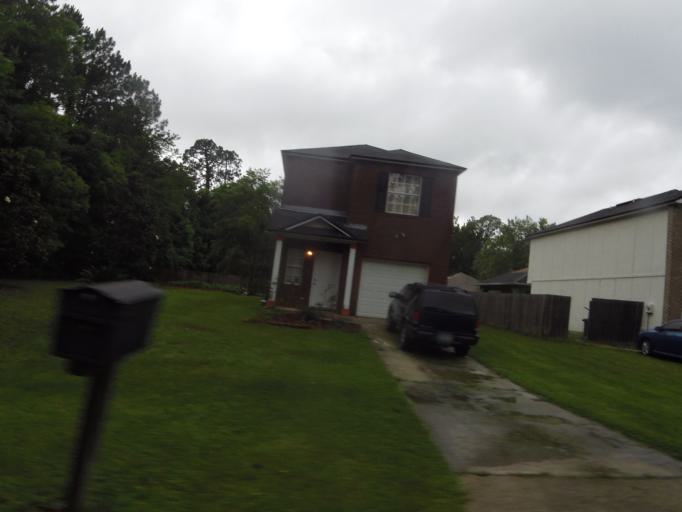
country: US
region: Florida
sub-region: Duval County
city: Jacksonville
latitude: 30.2758
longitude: -81.6216
